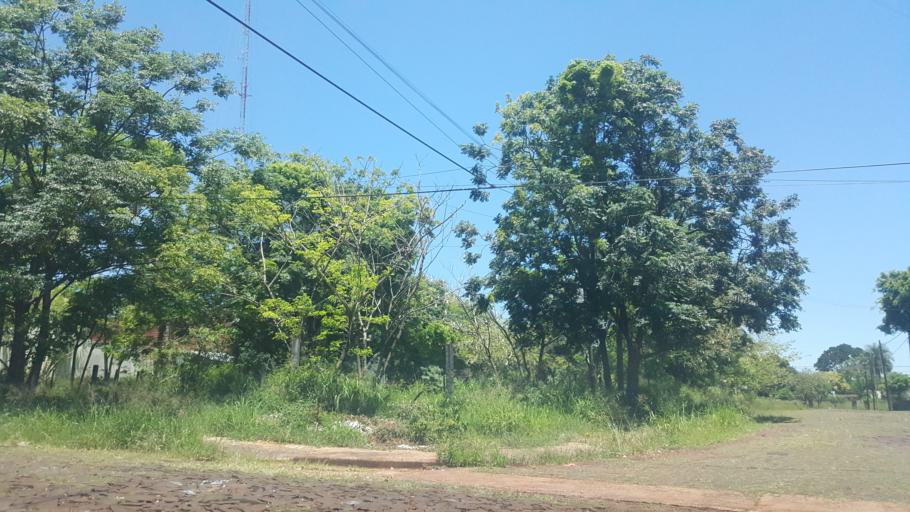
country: AR
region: Misiones
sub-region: Departamento de Capital
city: Posadas
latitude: -27.3912
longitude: -55.9143
